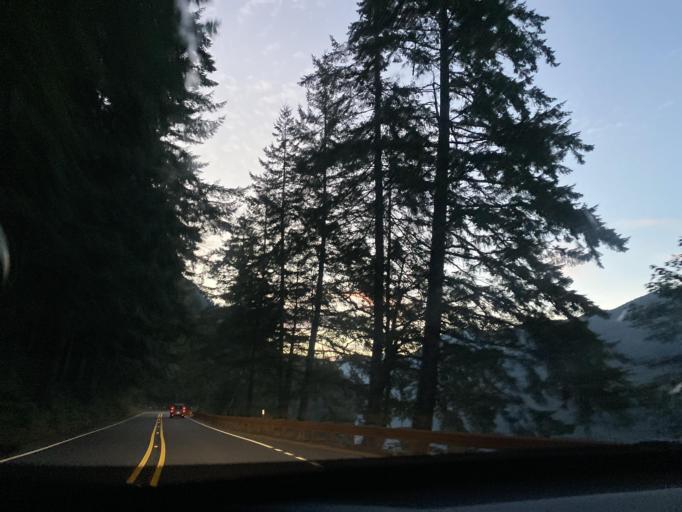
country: CA
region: British Columbia
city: Sooke
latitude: 48.0492
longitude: -123.8563
